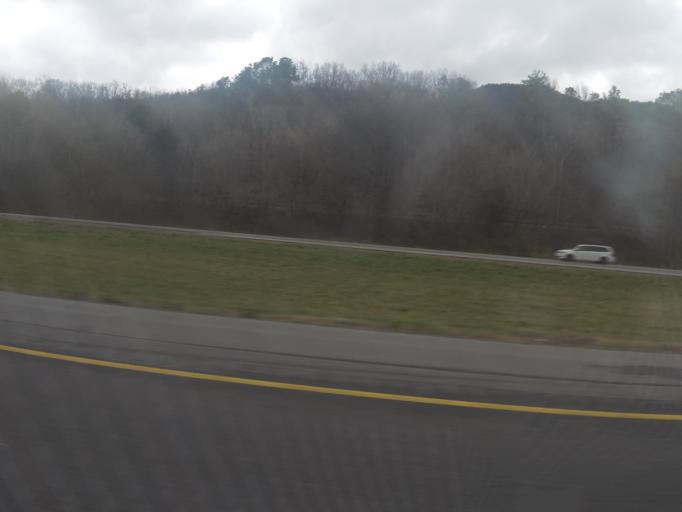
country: US
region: Tennessee
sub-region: Marion County
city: Jasper
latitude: 35.0061
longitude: -85.5191
